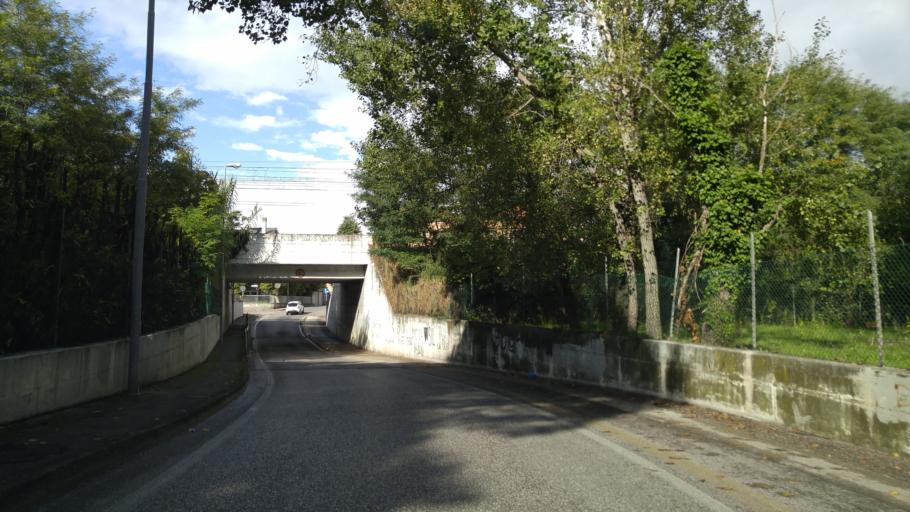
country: IT
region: The Marches
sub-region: Provincia di Pesaro e Urbino
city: Pesaro
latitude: 43.9074
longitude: 12.8961
